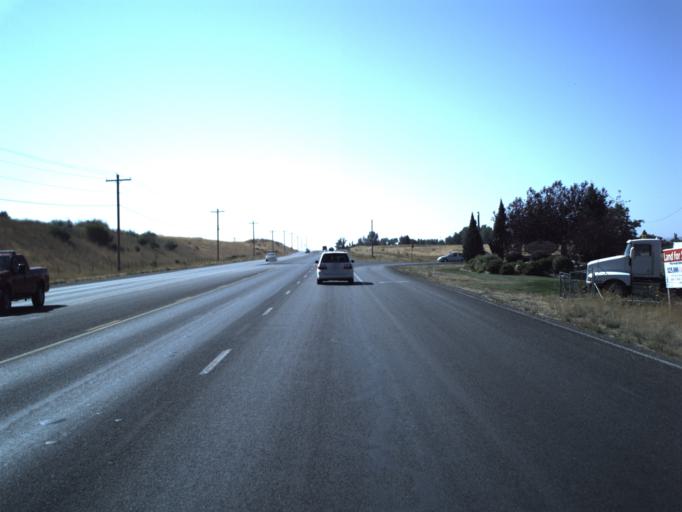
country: US
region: Utah
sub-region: Cache County
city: Hyrum
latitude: 41.6492
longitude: -111.8329
